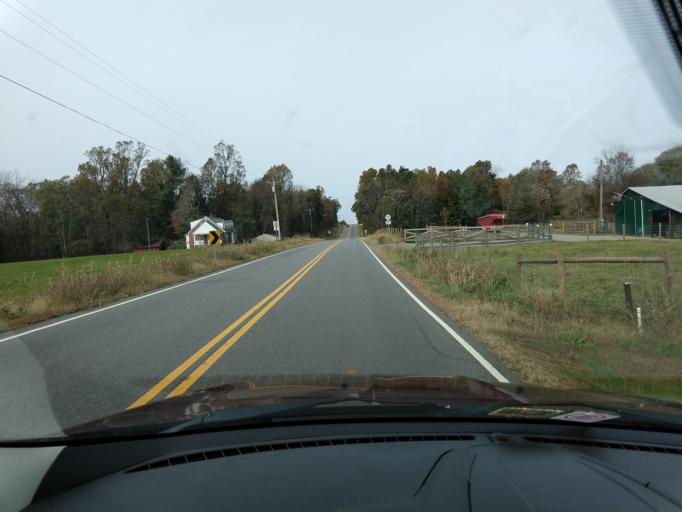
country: US
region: Virginia
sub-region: Franklin County
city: Union Hall
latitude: 36.9554
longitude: -79.5605
